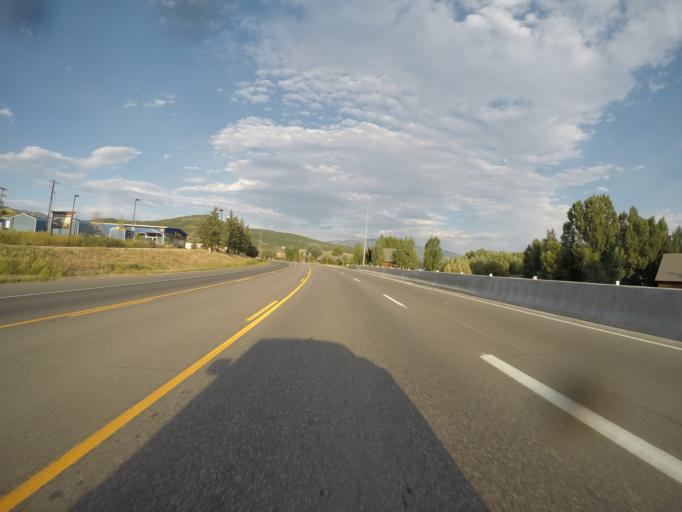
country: US
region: Colorado
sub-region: Routt County
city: Steamboat Springs
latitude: 40.5032
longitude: -106.8655
